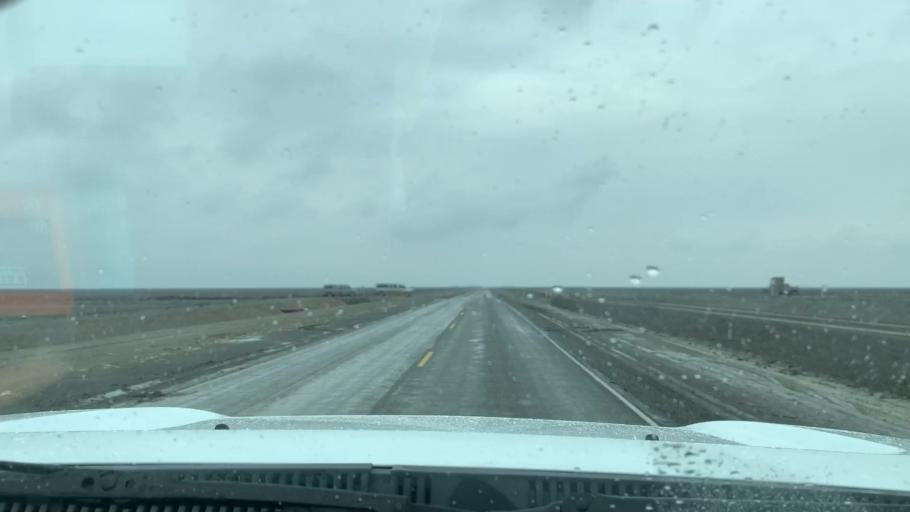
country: US
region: California
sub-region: Tulare County
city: Alpaugh
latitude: 35.9343
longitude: -119.5900
